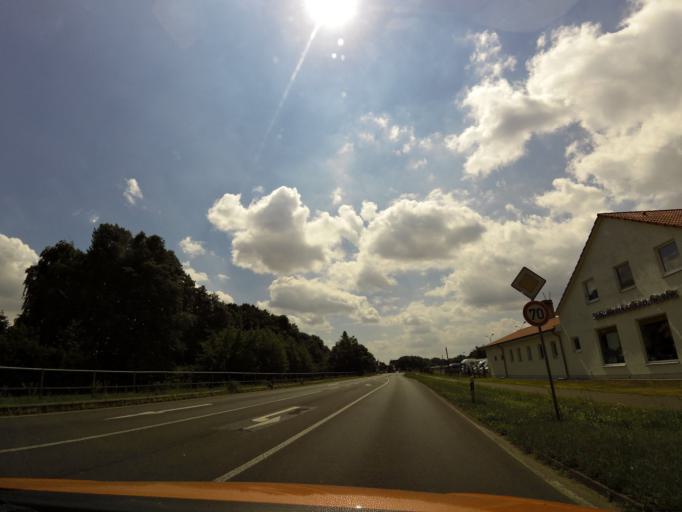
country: DE
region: Brandenburg
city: Wusterhausen
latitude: 52.8957
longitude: 12.4536
